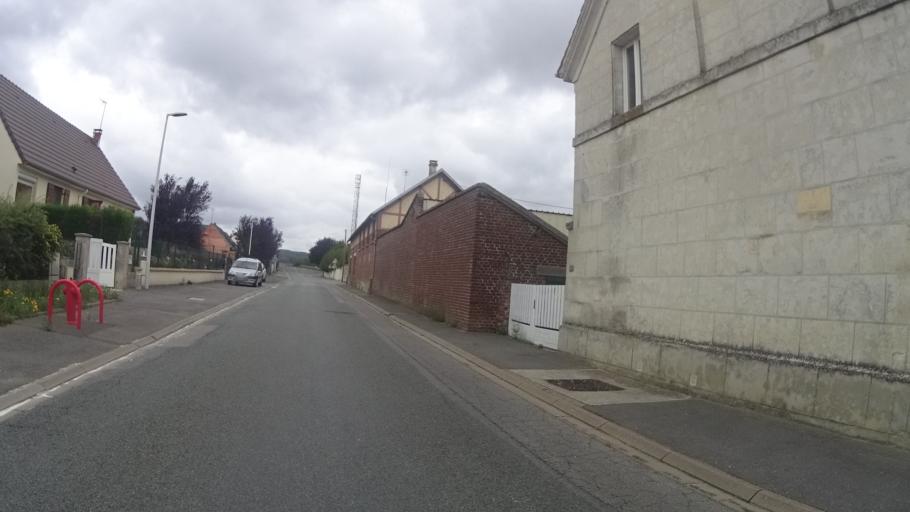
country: FR
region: Picardie
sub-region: Departement de l'Oise
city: Dreslincourt
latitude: 49.5174
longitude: 2.9510
